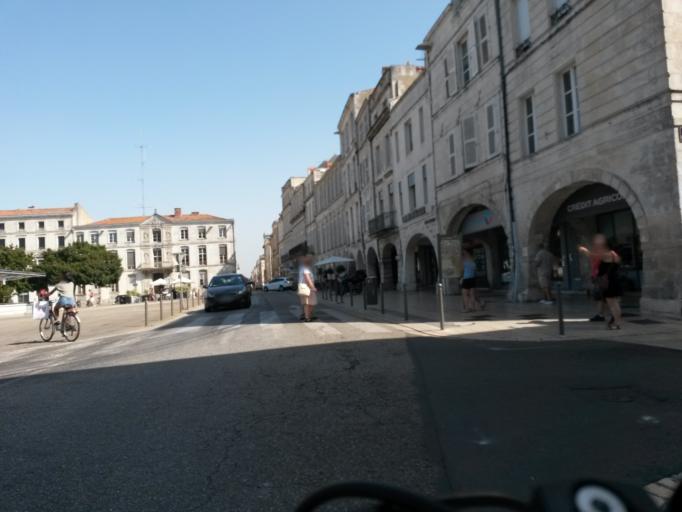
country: FR
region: Poitou-Charentes
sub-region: Departement de la Charente-Maritime
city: La Rochelle
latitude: 46.1620
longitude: -1.1527
